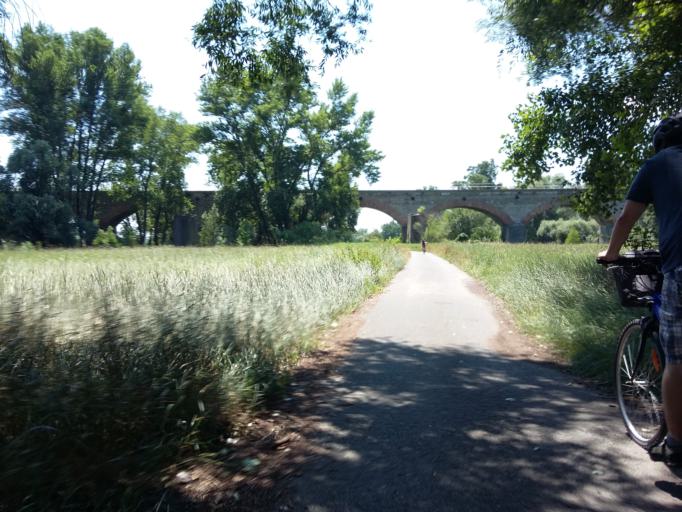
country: AT
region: Lower Austria
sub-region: Politischer Bezirk Ganserndorf
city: Marchegg
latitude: 48.2422
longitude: 16.9485
